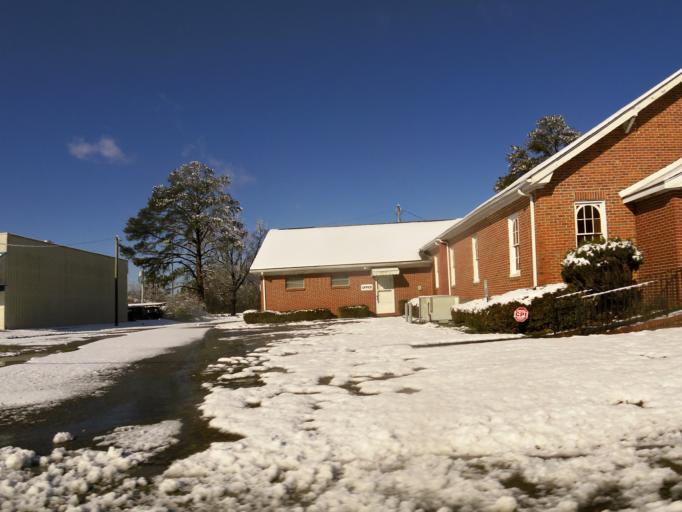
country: US
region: North Carolina
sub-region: Nash County
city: Sharpsburg
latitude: 35.8637
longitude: -77.8320
